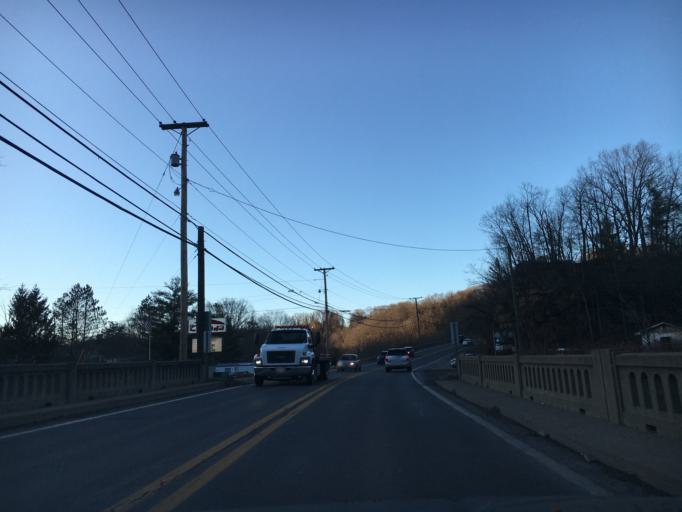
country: US
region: West Virginia
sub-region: Raleigh County
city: Beaver
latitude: 37.7572
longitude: -81.1568
